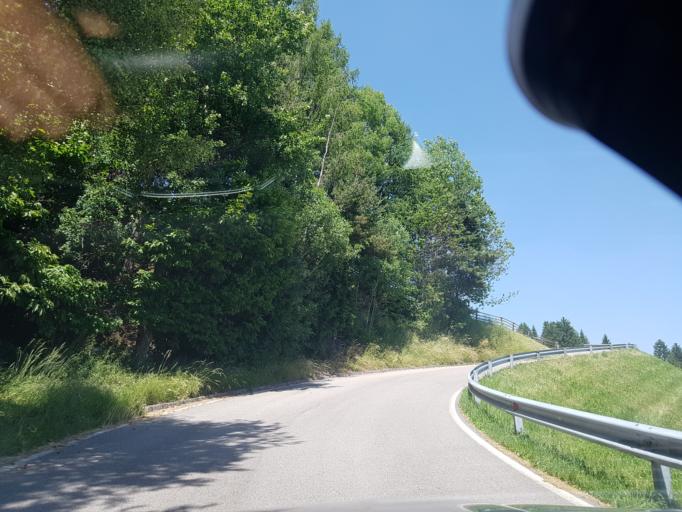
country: IT
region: Trentino-Alto Adige
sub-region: Bolzano
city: Villandro - Villanders
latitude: 46.6413
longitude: 11.5314
